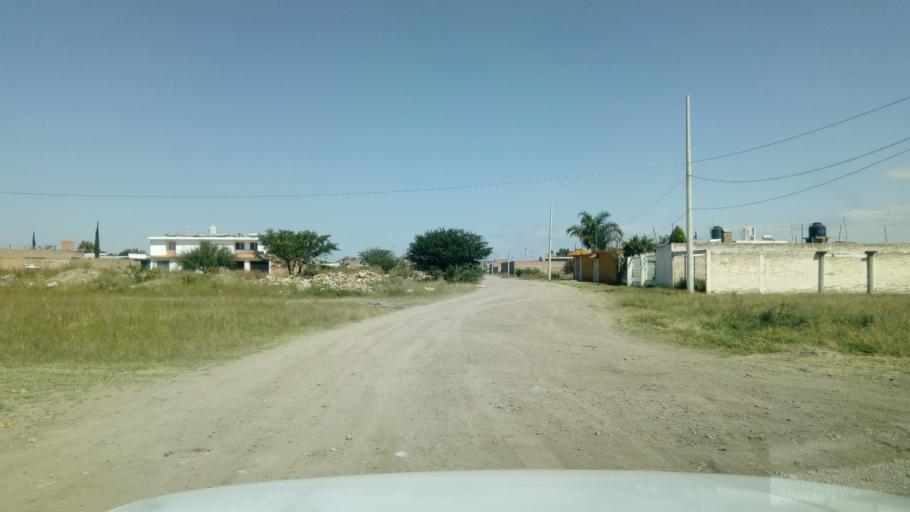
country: MX
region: Durango
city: Victoria de Durango
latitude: 23.9835
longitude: -104.6706
